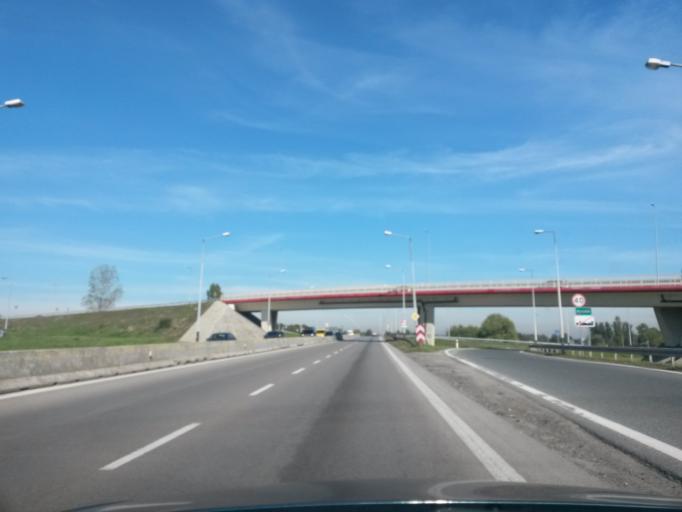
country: PL
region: Lesser Poland Voivodeship
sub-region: Powiat krakowski
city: Libertow
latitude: 49.9902
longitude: 19.9163
